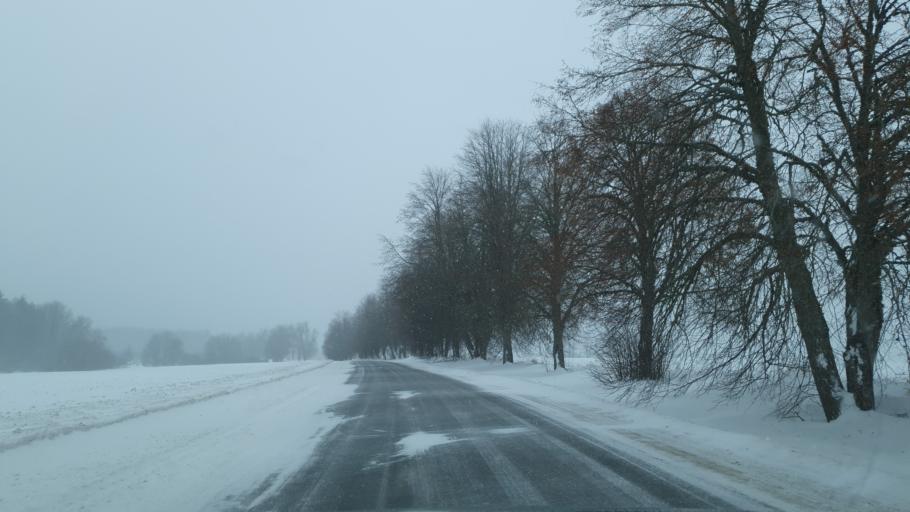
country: EE
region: Jogevamaa
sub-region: Jogeva linn
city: Jogeva
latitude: 58.7331
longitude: 26.5223
